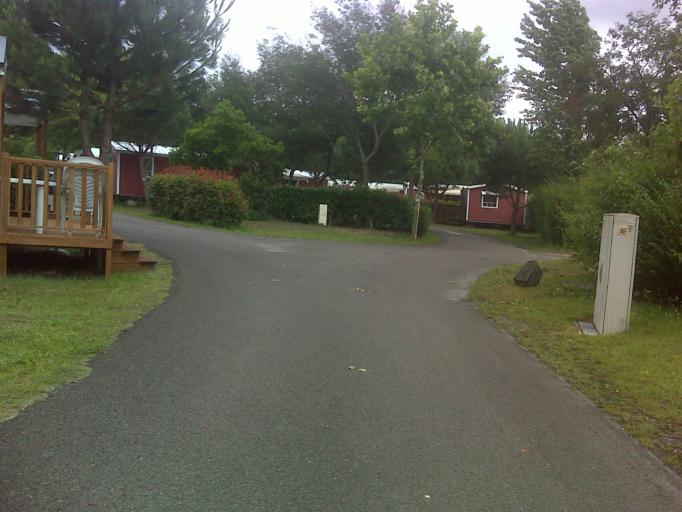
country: FR
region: Aquitaine
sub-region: Departement des Landes
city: Biscarrosse
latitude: 44.4362
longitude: -1.1566
